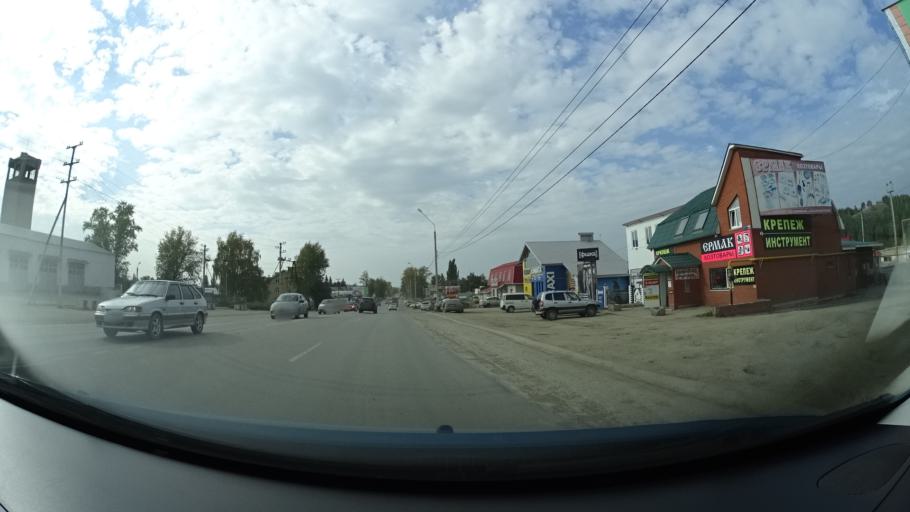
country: RU
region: Bashkortostan
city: Oktyabr'skiy
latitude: 54.4917
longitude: 53.4688
